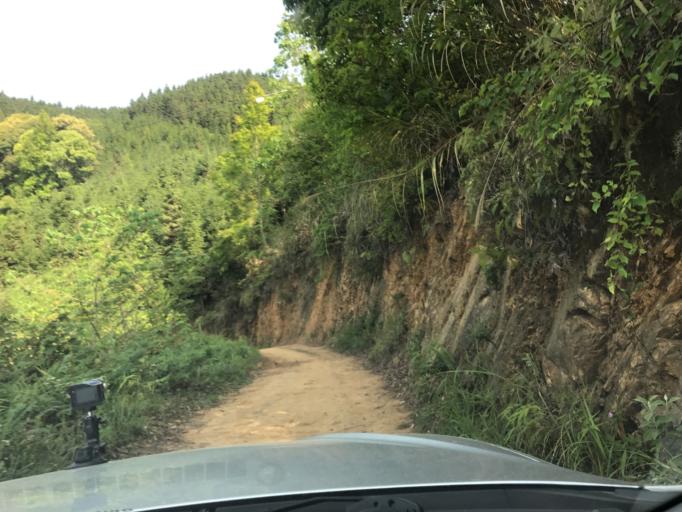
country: CN
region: Guangxi Zhuangzu Zizhiqu
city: Xinzhou
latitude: 24.9491
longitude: 105.8190
